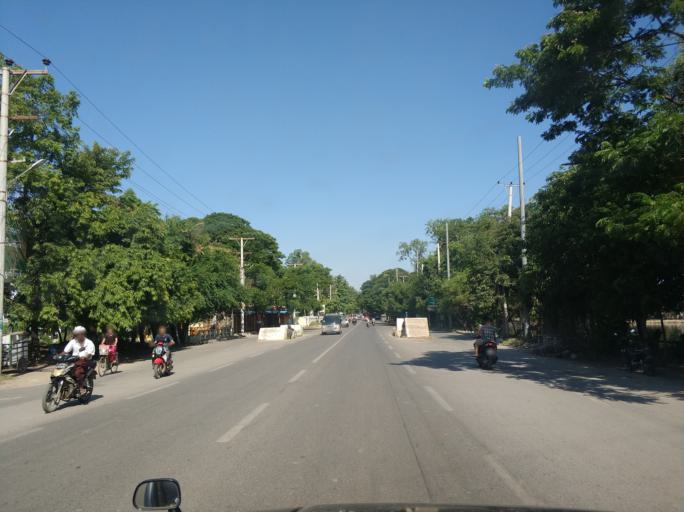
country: MM
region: Mandalay
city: Mandalay
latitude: 21.9710
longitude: 96.0619
